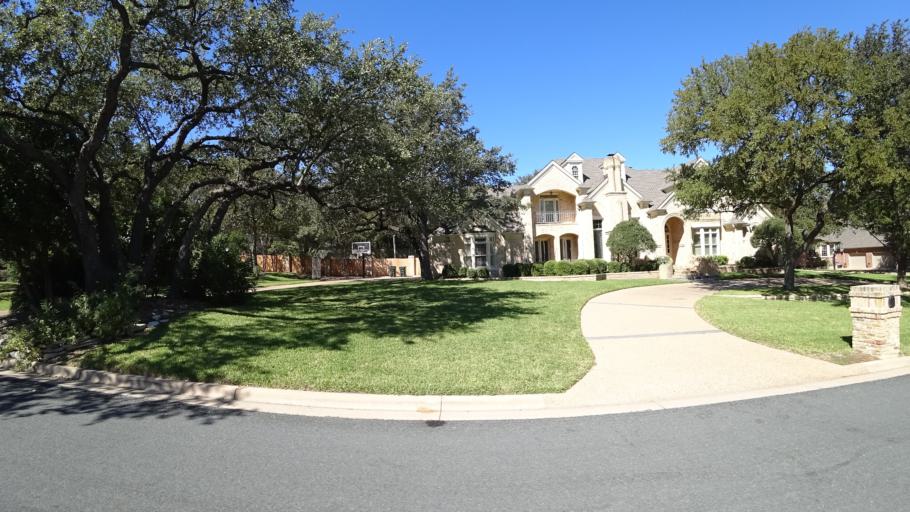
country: US
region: Texas
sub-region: Travis County
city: West Lake Hills
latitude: 30.3247
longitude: -97.7877
